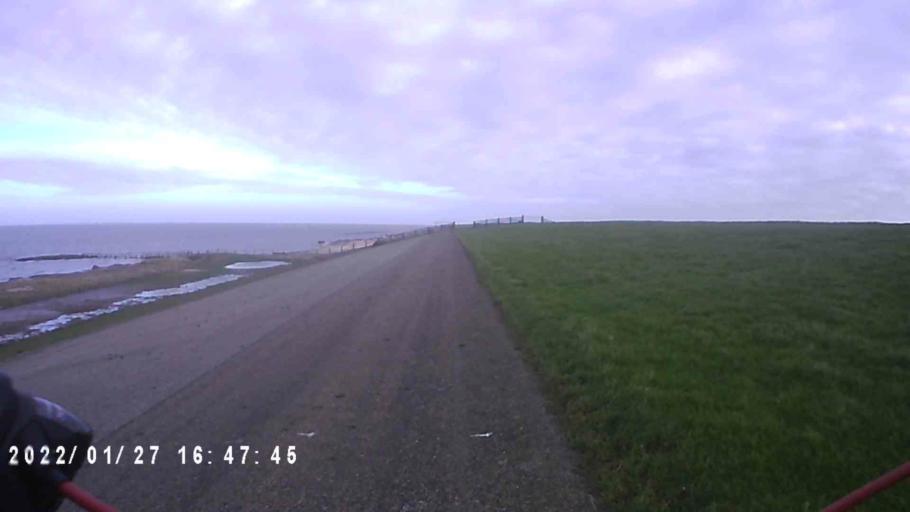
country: NL
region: Friesland
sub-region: Gemeente Dongeradeel
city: Ternaard
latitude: 53.4028
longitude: 6.0341
